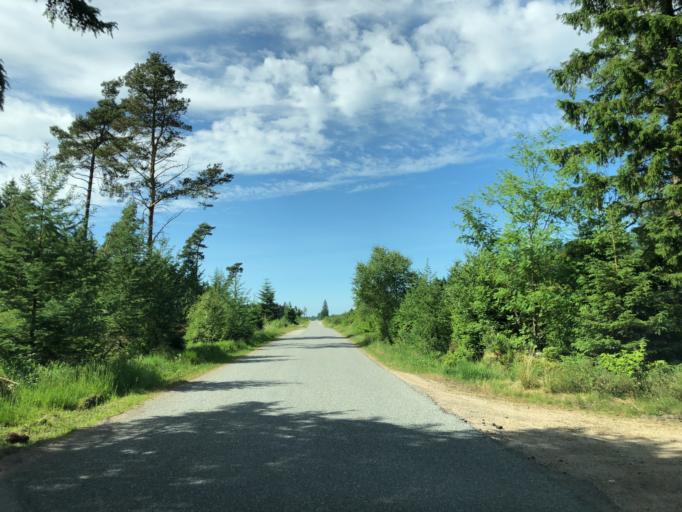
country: DK
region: Central Jutland
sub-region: Herning Kommune
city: Lind
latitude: 56.0461
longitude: 8.9311
